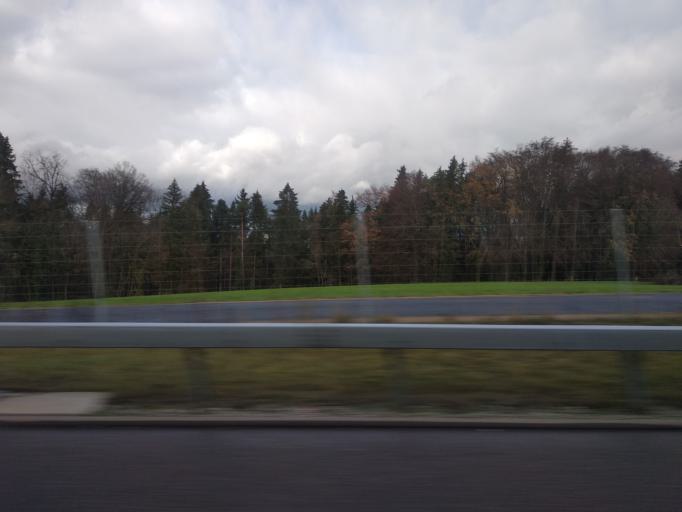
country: CH
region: Thurgau
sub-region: Frauenfeld District
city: Gachnang
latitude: 47.5304
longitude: 8.8614
